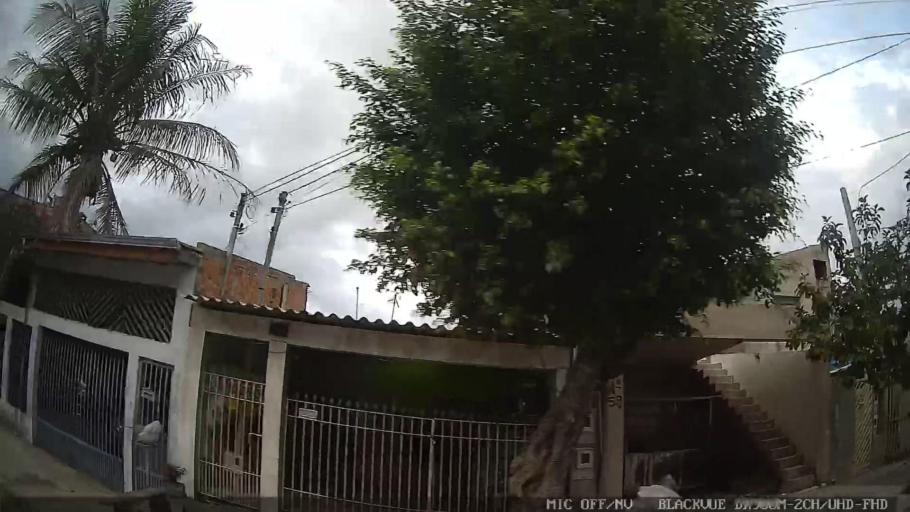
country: BR
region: Sao Paulo
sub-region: Indaiatuba
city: Indaiatuba
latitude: -23.1322
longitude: -47.2429
